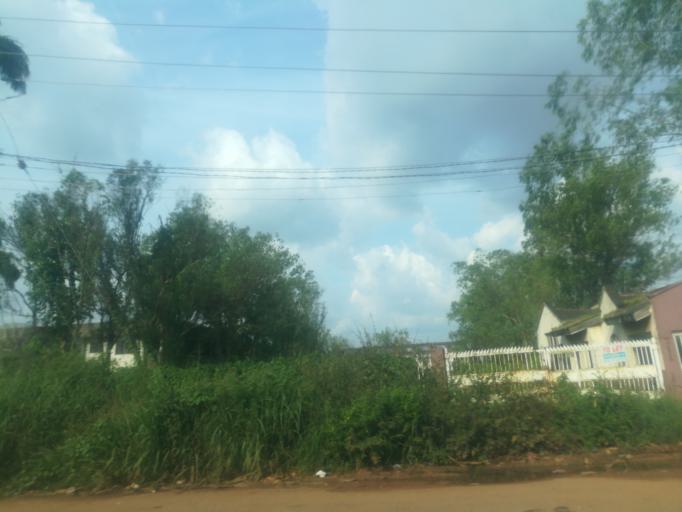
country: NG
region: Oyo
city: Ibadan
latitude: 7.3917
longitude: 3.8150
